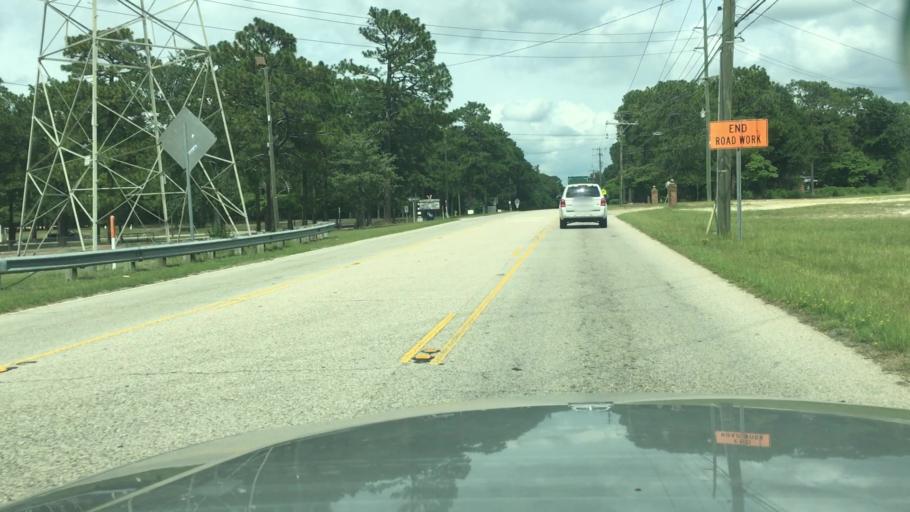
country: US
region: North Carolina
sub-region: Cumberland County
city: Fayetteville
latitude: 35.0199
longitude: -78.9118
